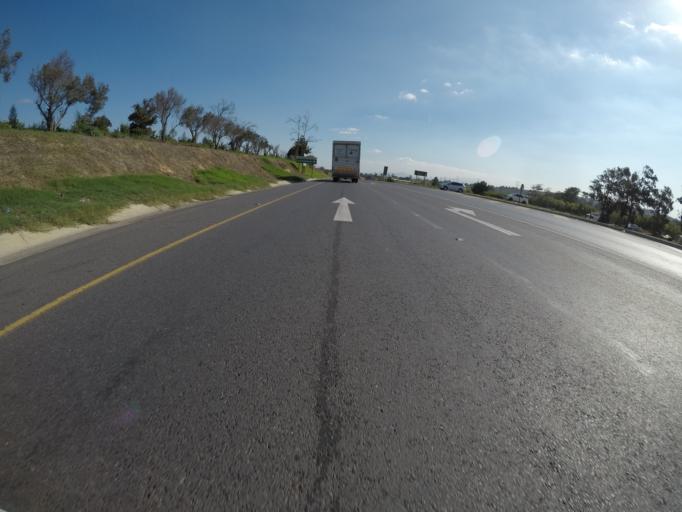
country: ZA
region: Western Cape
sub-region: City of Cape Town
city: Kraaifontein
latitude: -33.8873
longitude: 18.7464
